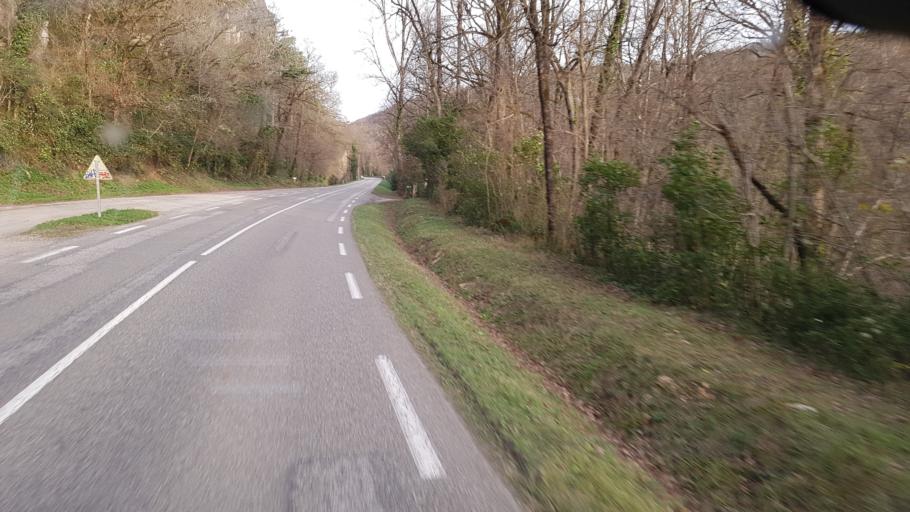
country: FR
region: Midi-Pyrenees
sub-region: Departement du Tarn-et-Garonne
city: Montricoux
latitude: 44.0578
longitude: 1.6659
